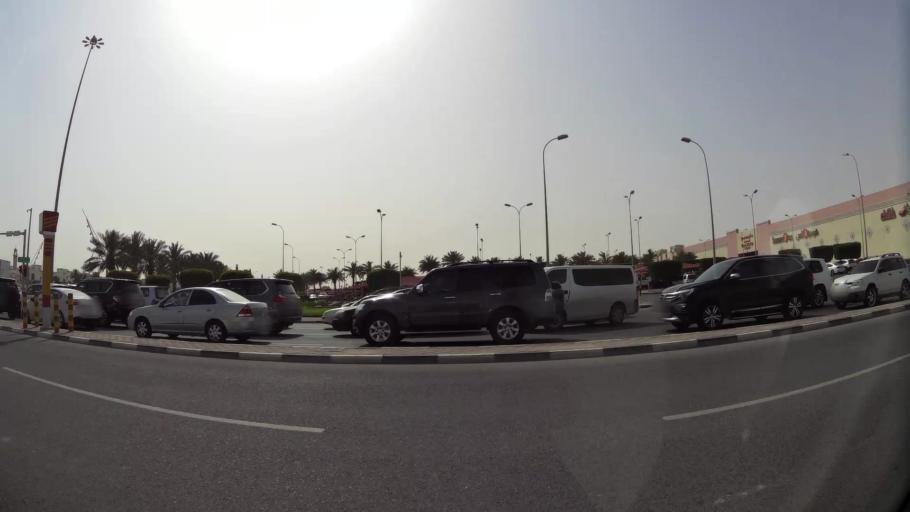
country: QA
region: Baladiyat ar Rayyan
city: Ar Rayyan
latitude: 25.2562
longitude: 51.4401
